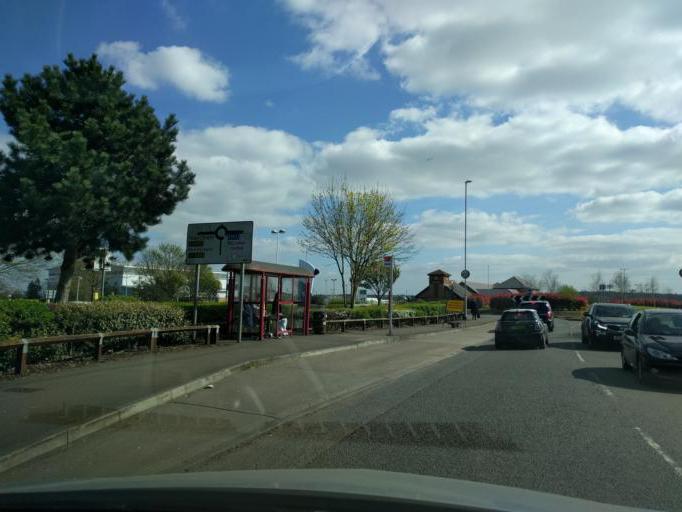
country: GB
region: England
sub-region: Northamptonshire
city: Northampton
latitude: 52.2386
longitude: -0.9352
